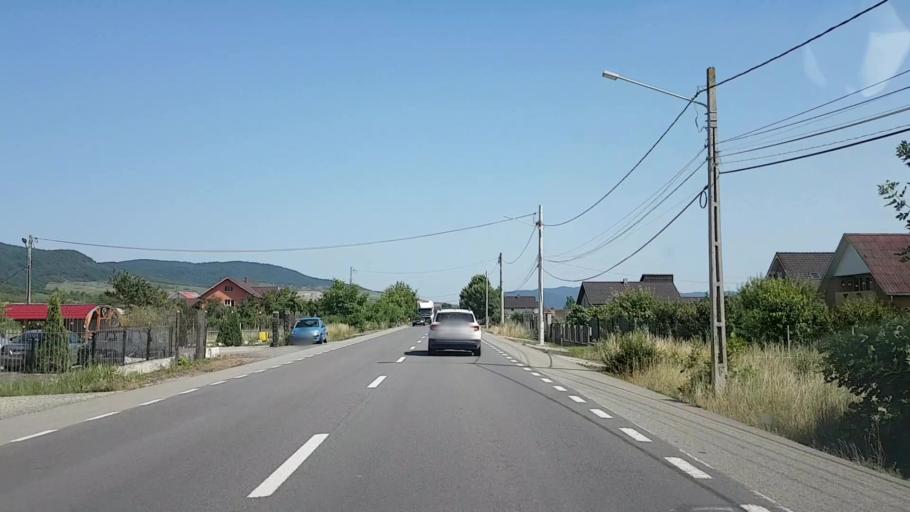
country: RO
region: Bistrita-Nasaud
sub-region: Comuna Sieu-Magherus
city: Sieu-Magherus
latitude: 47.0985
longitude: 24.3640
